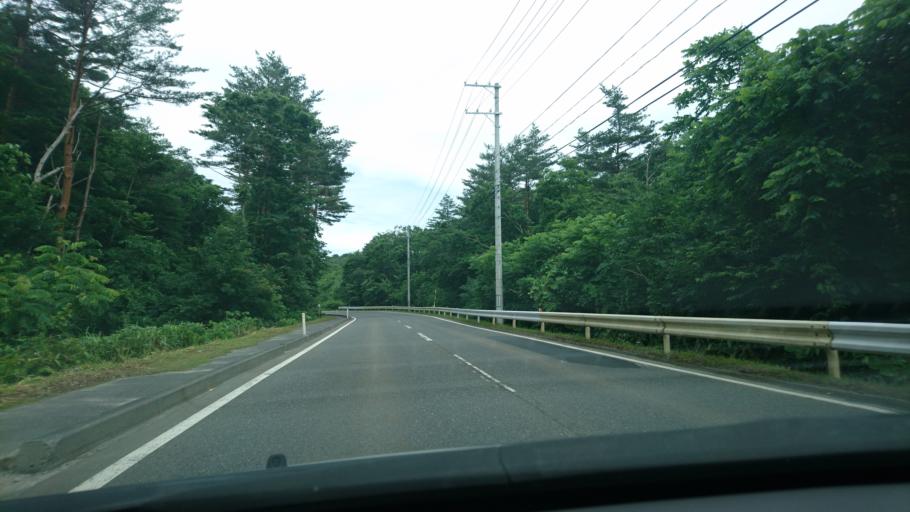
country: JP
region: Iwate
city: Miyako
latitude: 39.9441
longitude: 141.8417
